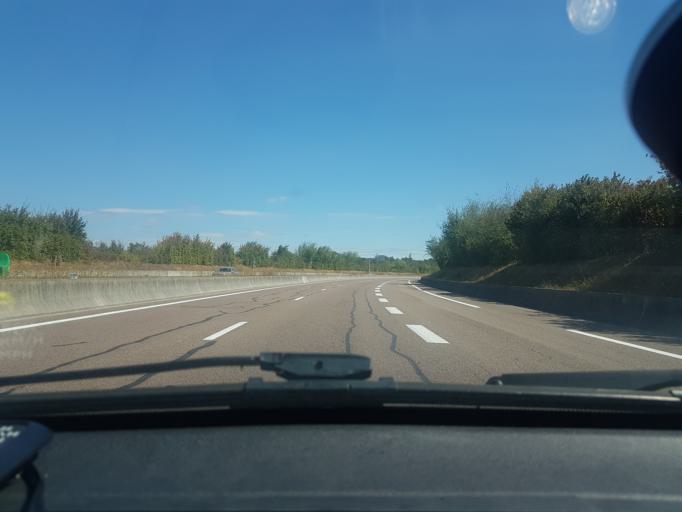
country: FR
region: Bourgogne
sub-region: Departement de la Cote-d'Or
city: Varois-et-Chaignot
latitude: 47.3456
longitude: 5.1414
